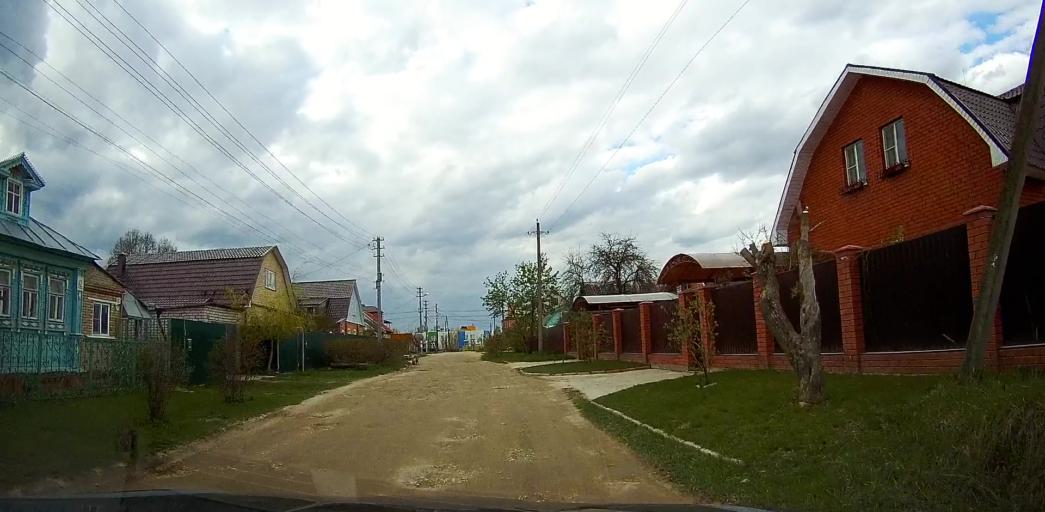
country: RU
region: Moskovskaya
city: Pavlovskiy Posad
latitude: 55.7786
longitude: 38.6318
